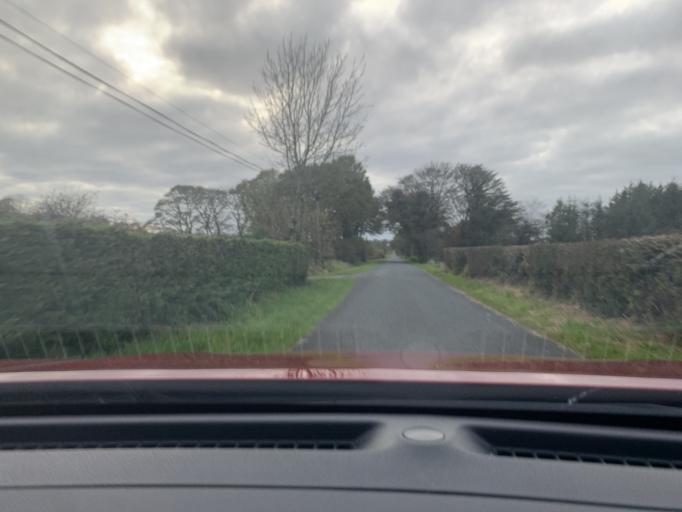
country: IE
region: Connaught
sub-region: Sligo
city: Tobercurry
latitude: 54.0290
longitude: -8.6763
